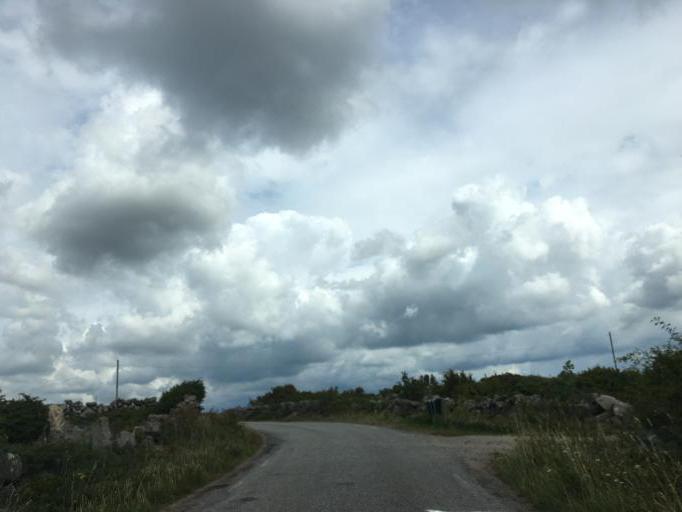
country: SE
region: Vaestra Goetaland
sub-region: Sotenas Kommun
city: Kungshamn
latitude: 58.4081
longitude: 11.2523
